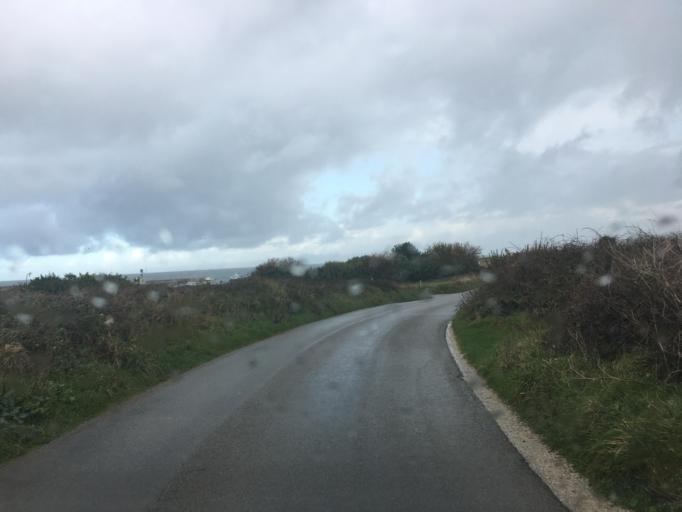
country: FR
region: Lower Normandy
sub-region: Departement de la Manche
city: Reville
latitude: 49.6916
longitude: -1.2778
